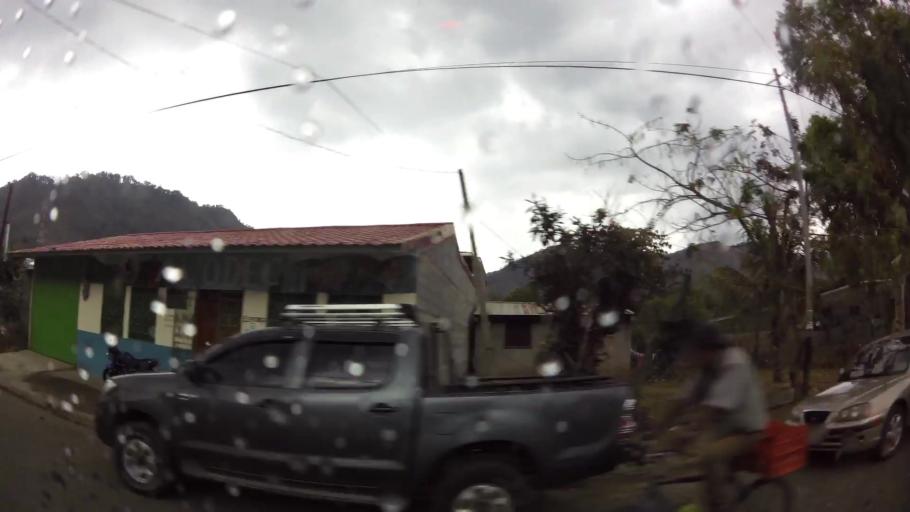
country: NI
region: Jinotega
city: Jinotega
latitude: 13.1020
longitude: -86.0039
